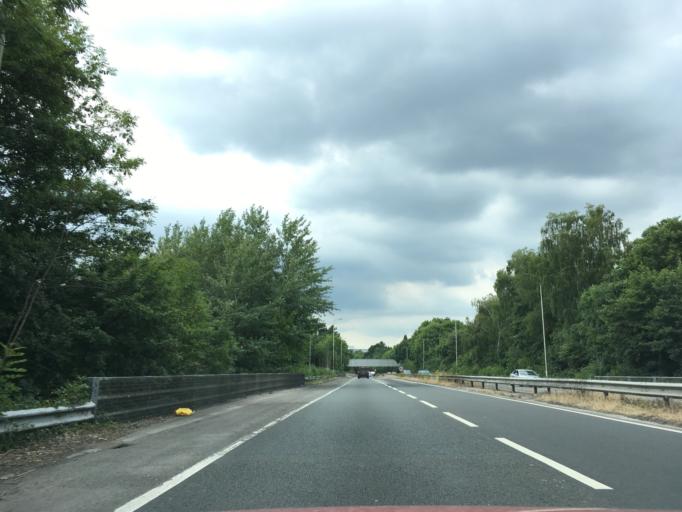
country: GB
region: Wales
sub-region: Cardiff
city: Cardiff
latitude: 51.5025
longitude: -3.1736
